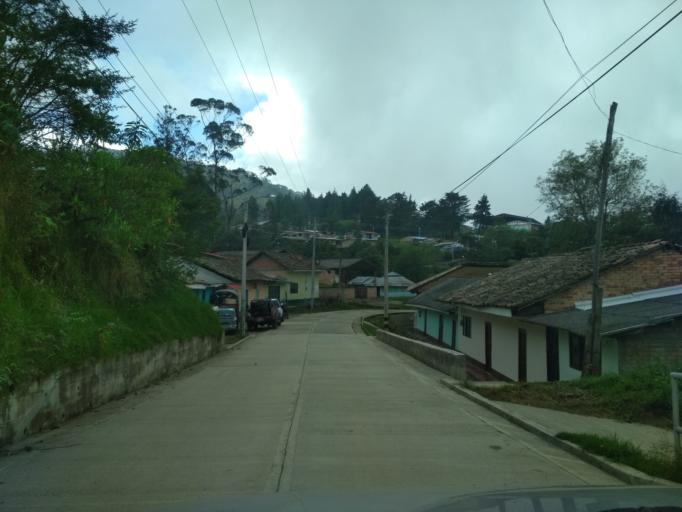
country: CO
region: Cauca
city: Paispamba
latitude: 2.2552
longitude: -76.6135
